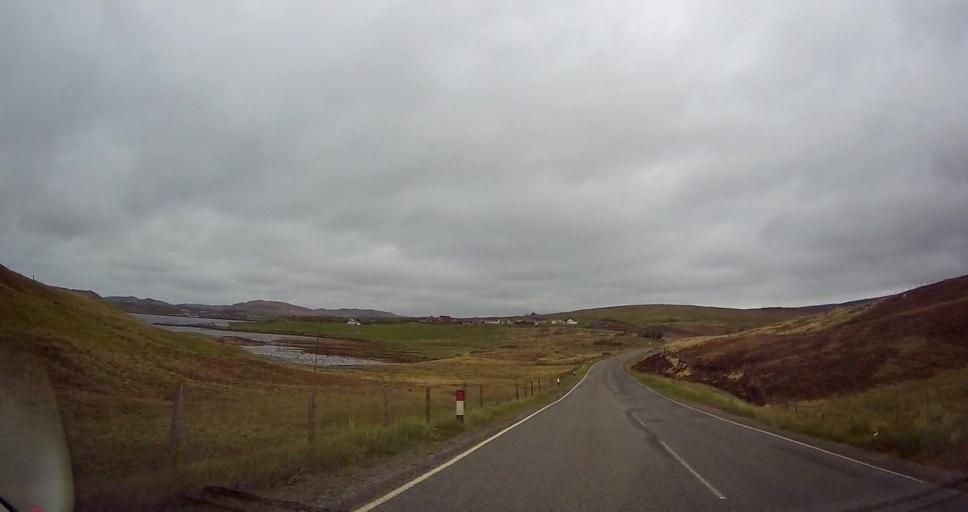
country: GB
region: Scotland
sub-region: Shetland Islands
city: Lerwick
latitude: 60.3803
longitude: -1.3424
